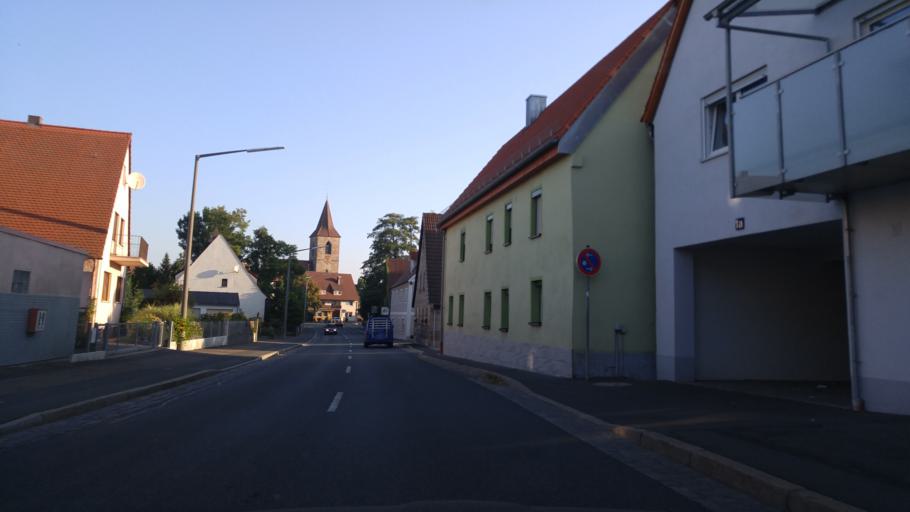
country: DE
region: Bavaria
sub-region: Regierungsbezirk Mittelfranken
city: Erlangen
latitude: 49.5517
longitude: 10.9886
